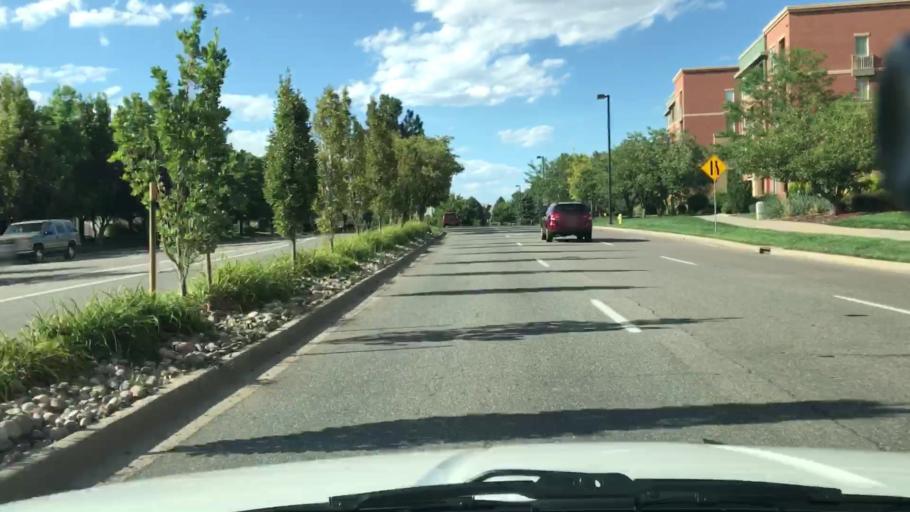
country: US
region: Colorado
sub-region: Arapahoe County
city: Greenwood Village
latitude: 39.6278
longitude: -104.9110
